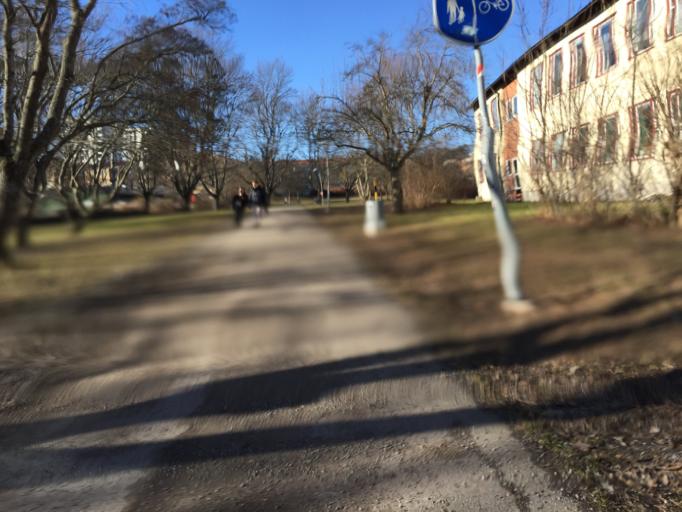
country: SE
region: Stockholm
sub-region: Stockholms Kommun
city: Bromma
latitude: 59.3626
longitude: 17.8815
